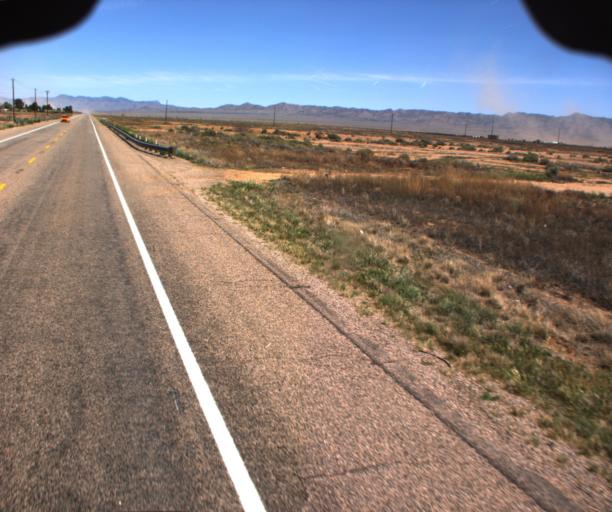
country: US
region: Arizona
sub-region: Mohave County
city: New Kingman-Butler
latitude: 35.2832
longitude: -113.9476
